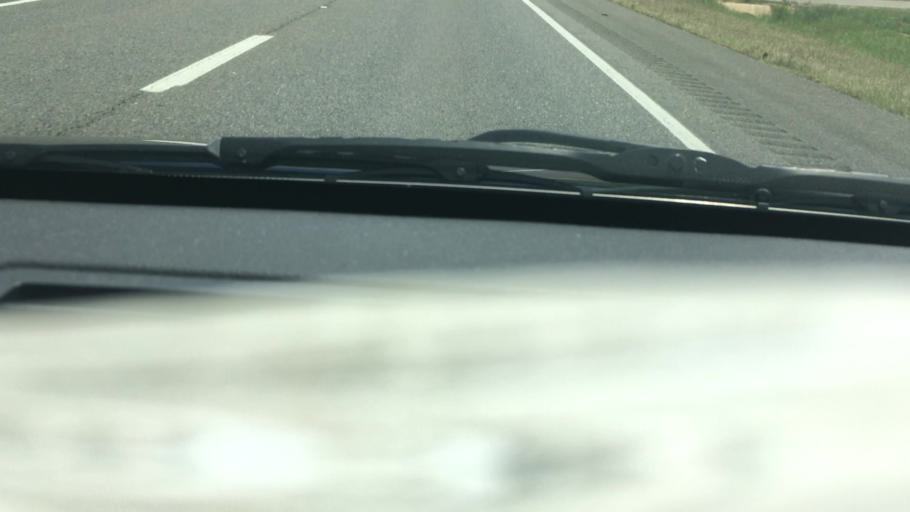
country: US
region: Alabama
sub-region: Pickens County
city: Gordo
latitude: 33.2794
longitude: -87.7844
